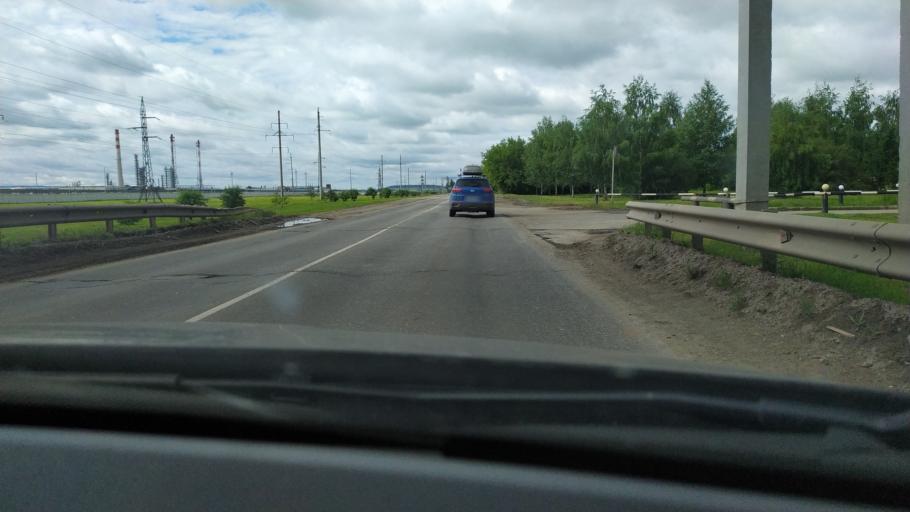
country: RU
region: Perm
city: Kondratovo
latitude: 57.9296
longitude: 56.1206
